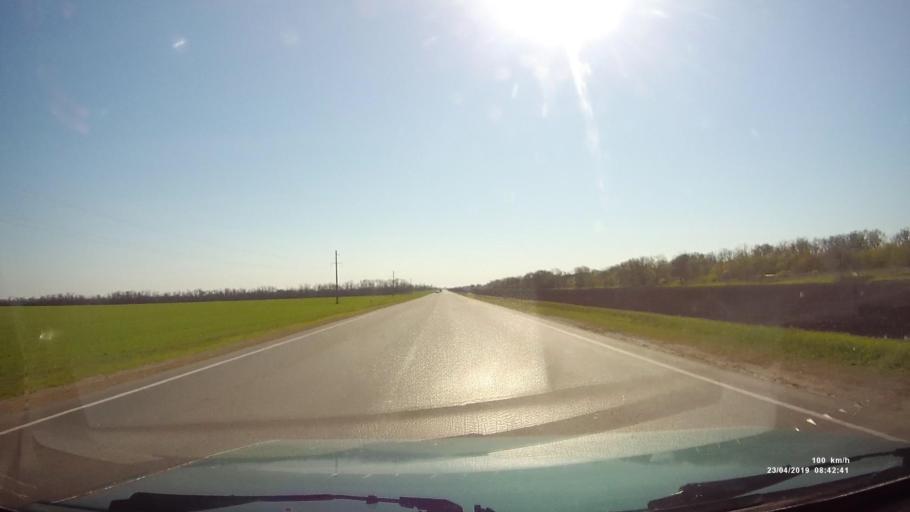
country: RU
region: Rostov
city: Gigant
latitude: 46.5228
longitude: 41.2756
